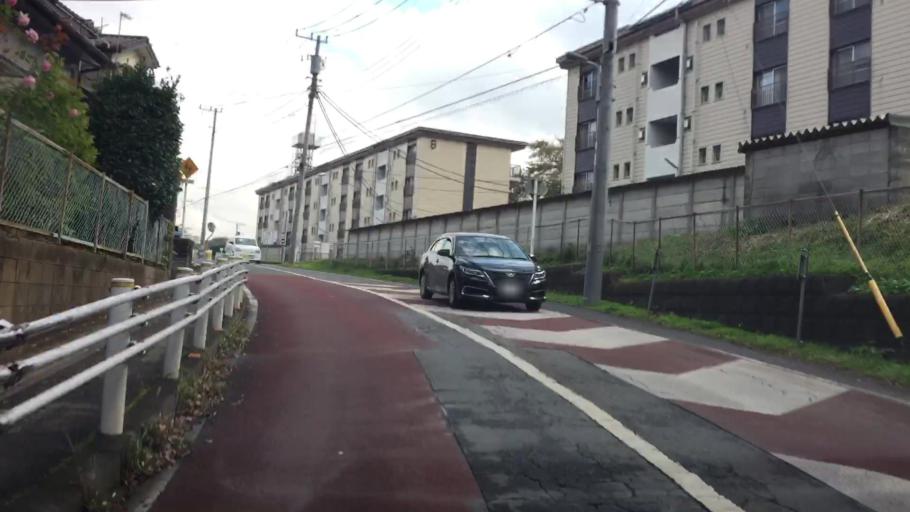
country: JP
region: Chiba
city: Kashiwa
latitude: 35.8340
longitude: 139.9490
